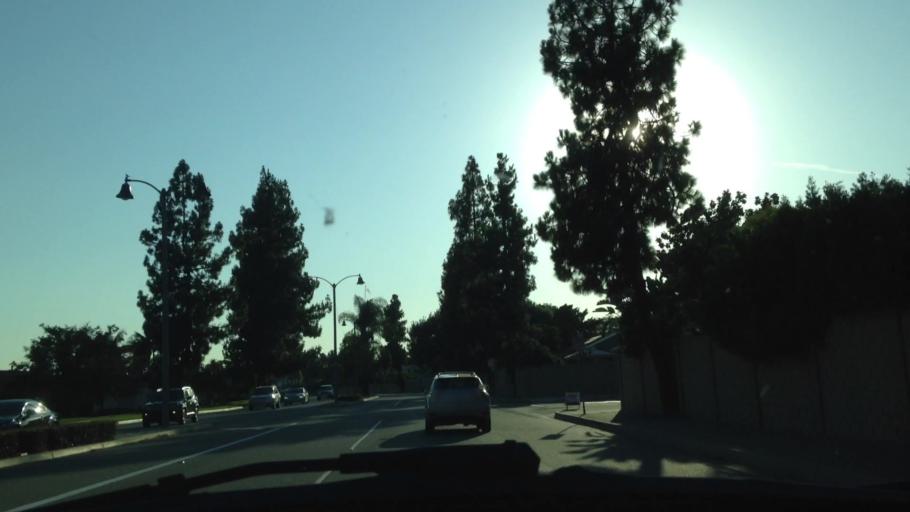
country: US
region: California
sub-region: Orange County
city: Placentia
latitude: 33.8893
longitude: -117.8571
